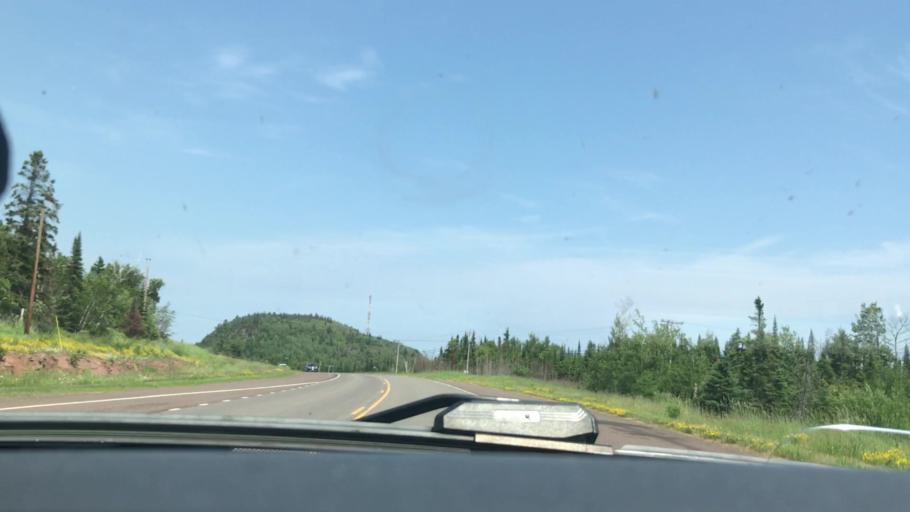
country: US
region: Minnesota
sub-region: Lake County
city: Silver Bay
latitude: 47.3140
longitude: -91.2284
